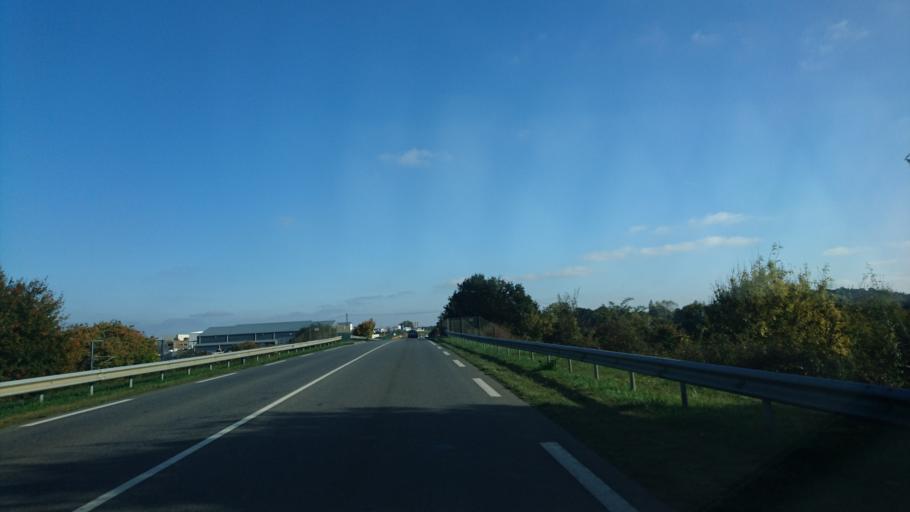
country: FR
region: Brittany
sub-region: Departement d'Ille-et-Vilaine
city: Saint-Jacques-de-la-Lande
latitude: 48.0539
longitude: -1.7291
